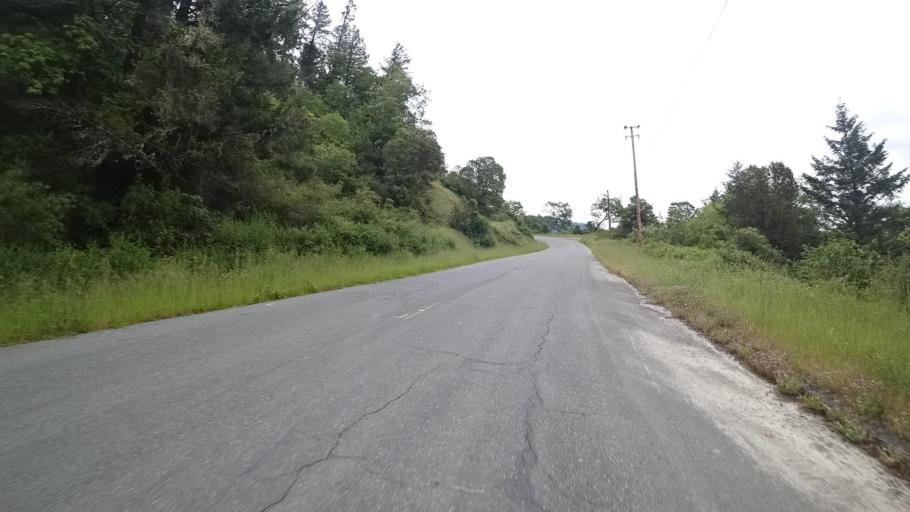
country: US
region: California
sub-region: Humboldt County
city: Willow Creek
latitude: 41.1023
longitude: -123.7116
